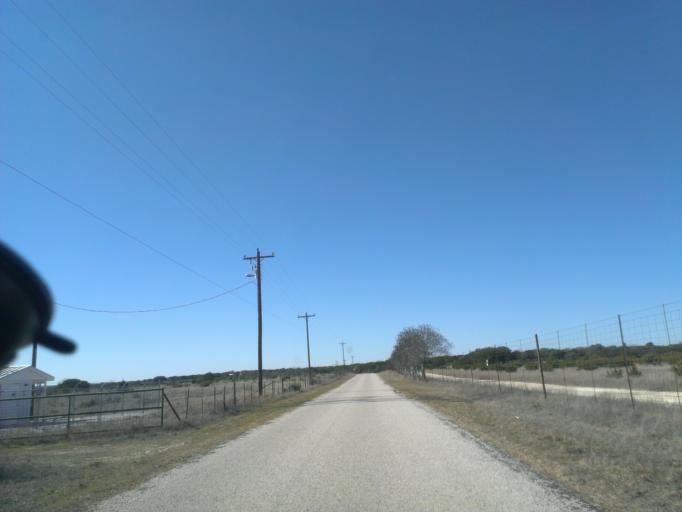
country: US
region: Texas
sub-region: Lampasas County
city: Kempner
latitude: 30.9357
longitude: -98.0234
